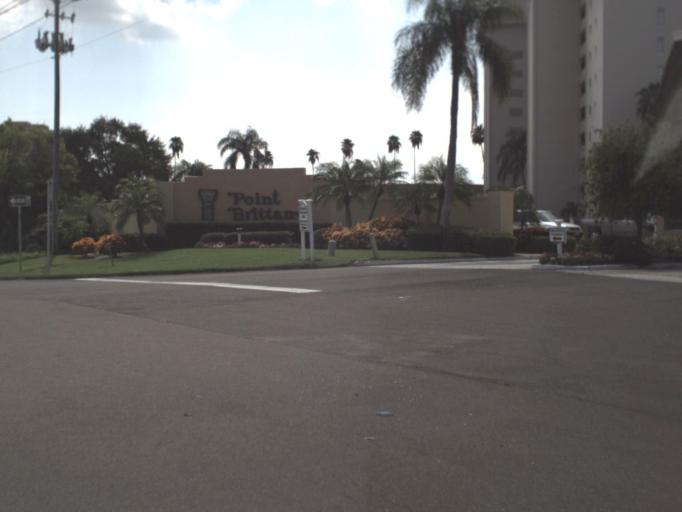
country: US
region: Florida
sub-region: Pinellas County
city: Tierra Verde
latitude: 27.7158
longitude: -82.7043
